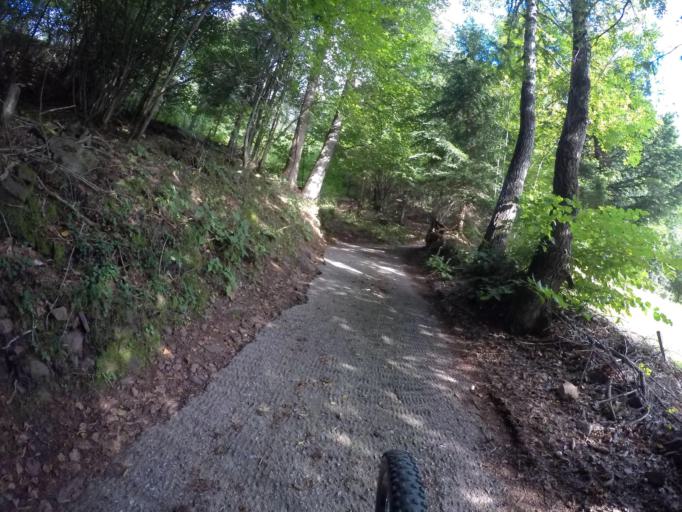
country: IT
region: Friuli Venezia Giulia
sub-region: Provincia di Udine
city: Paularo
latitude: 46.5407
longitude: 13.1123
